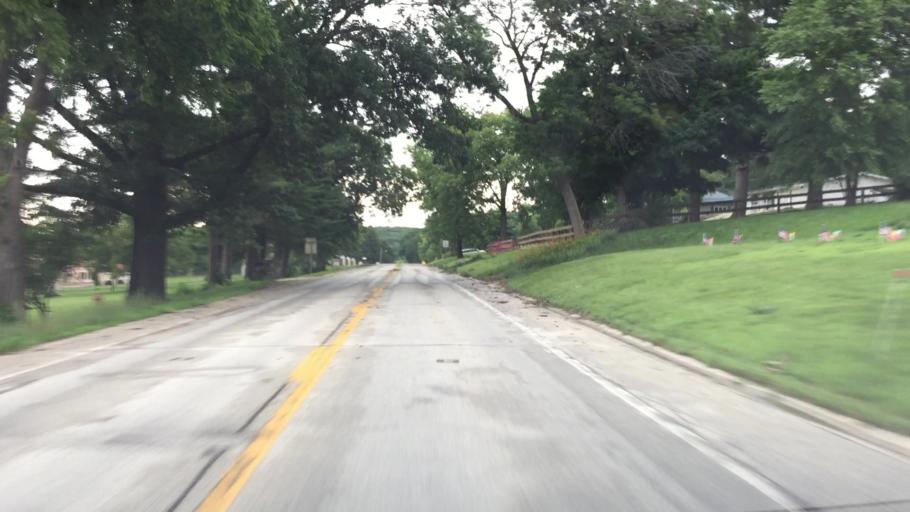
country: US
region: Illinois
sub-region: Hancock County
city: Hamilton
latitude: 40.3997
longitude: -91.3518
